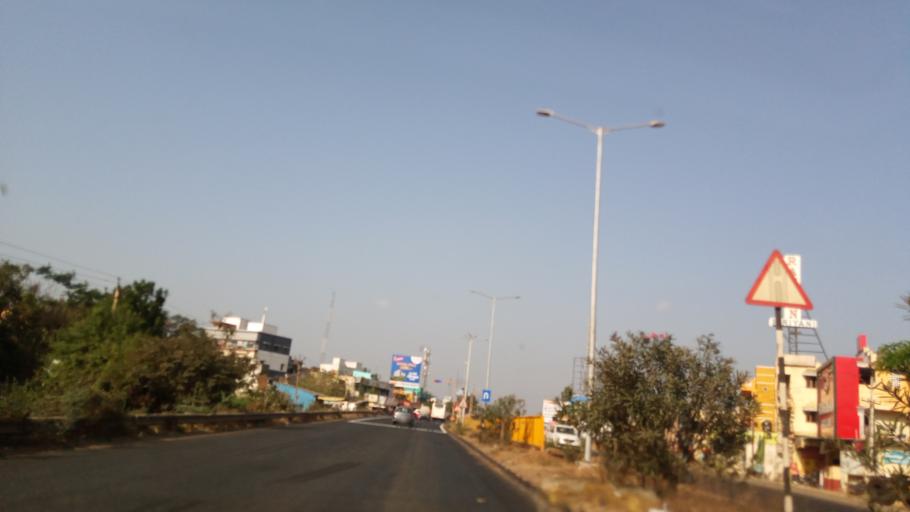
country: IN
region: Tamil Nadu
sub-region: Kancheepuram
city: Nandambakkam
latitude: 13.0147
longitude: 80.0032
